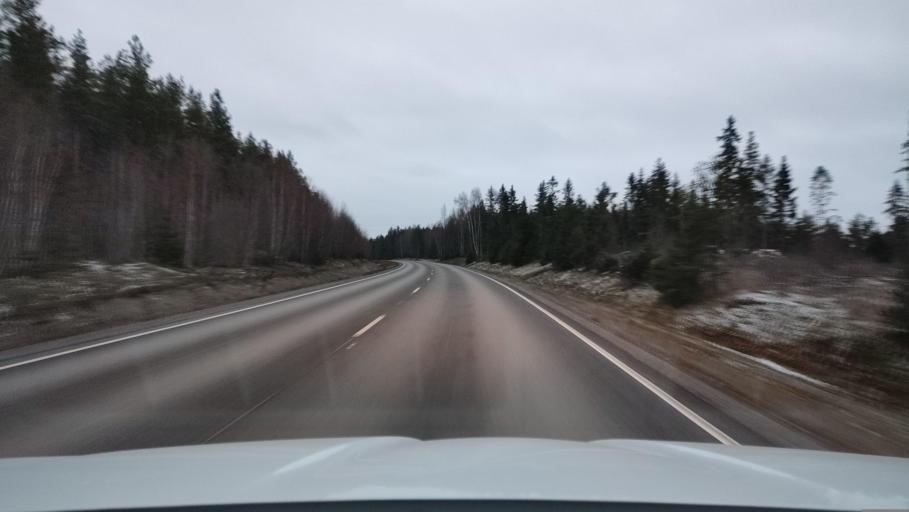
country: FI
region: Ostrobothnia
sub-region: Vaasa
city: Replot
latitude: 63.2089
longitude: 21.4377
